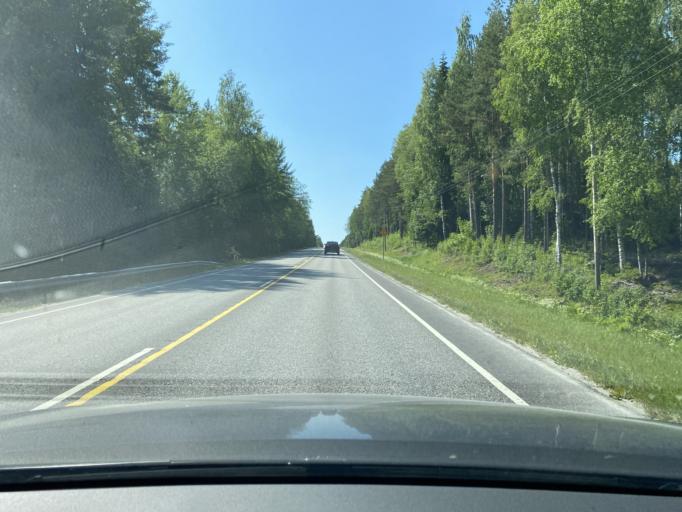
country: FI
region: Pirkanmaa
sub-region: Tampere
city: Nokia
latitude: 61.4283
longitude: 23.3698
